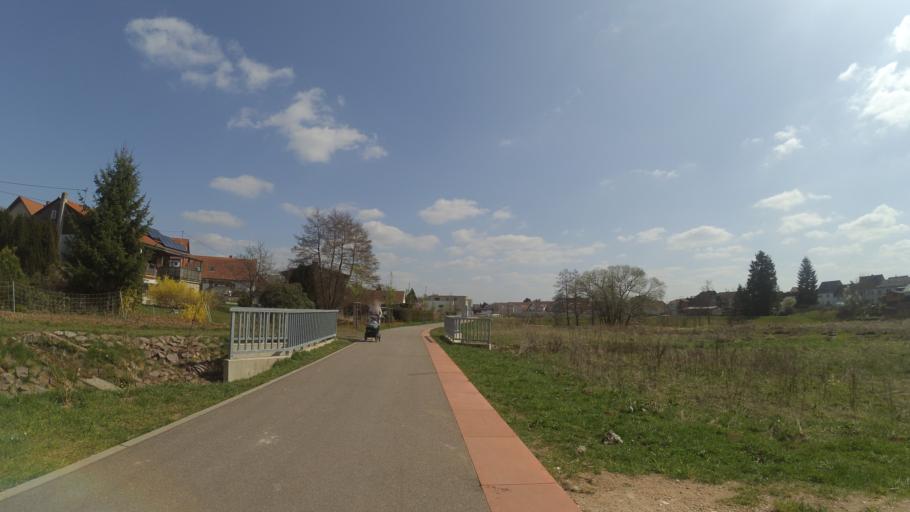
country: DE
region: Saarland
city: Oberthal
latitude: 49.5117
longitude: 7.0856
